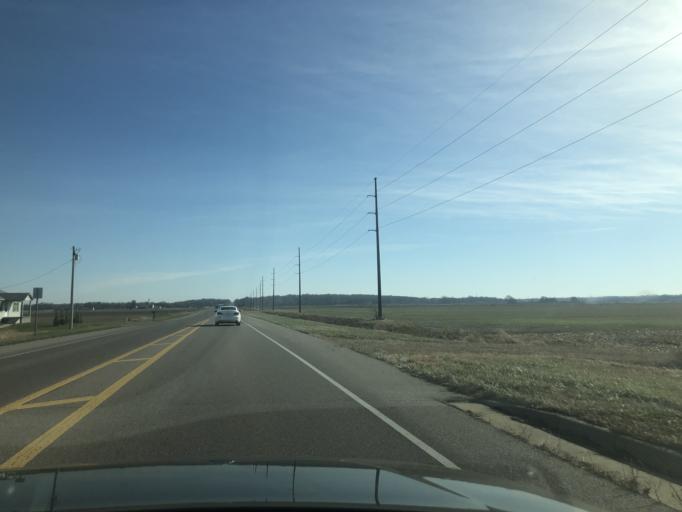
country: US
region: Indiana
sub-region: Warrick County
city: Newburgh
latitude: 37.9912
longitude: -87.4374
